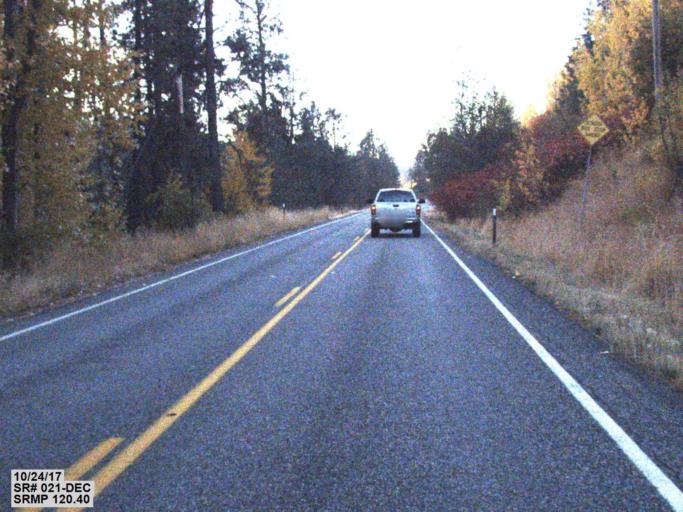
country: US
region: Washington
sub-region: Okanogan County
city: Coulee Dam
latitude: 48.1271
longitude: -118.6926
